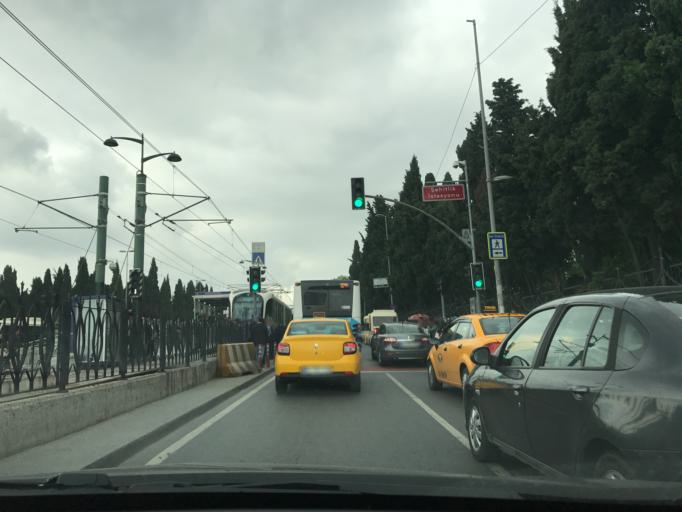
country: TR
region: Istanbul
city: Istanbul
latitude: 41.0339
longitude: 28.9291
